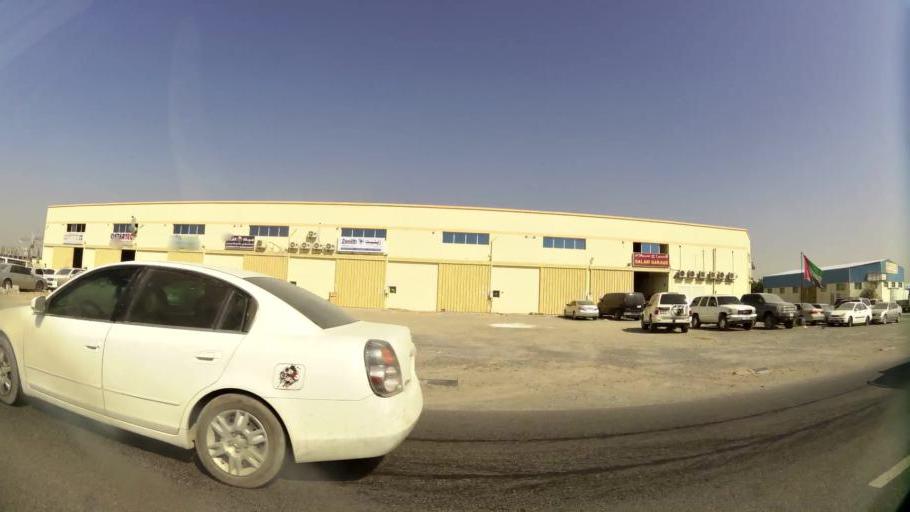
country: AE
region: Ajman
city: Ajman
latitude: 25.4322
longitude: 55.5361
